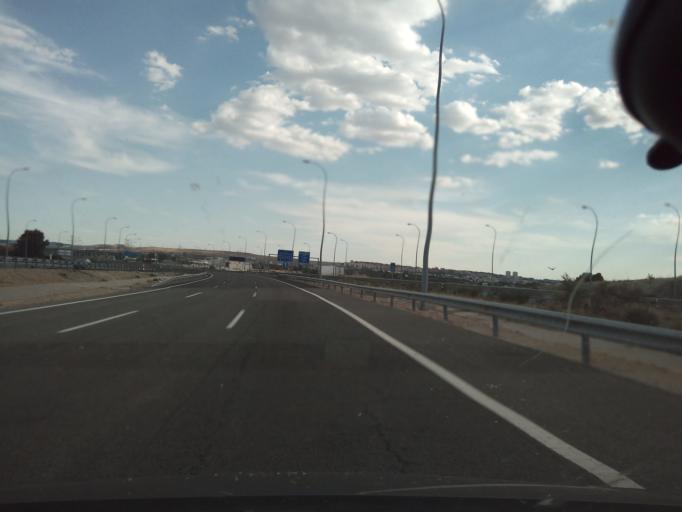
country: ES
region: Madrid
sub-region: Provincia de Madrid
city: San Fernando de Henares
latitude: 40.4597
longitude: -3.5200
